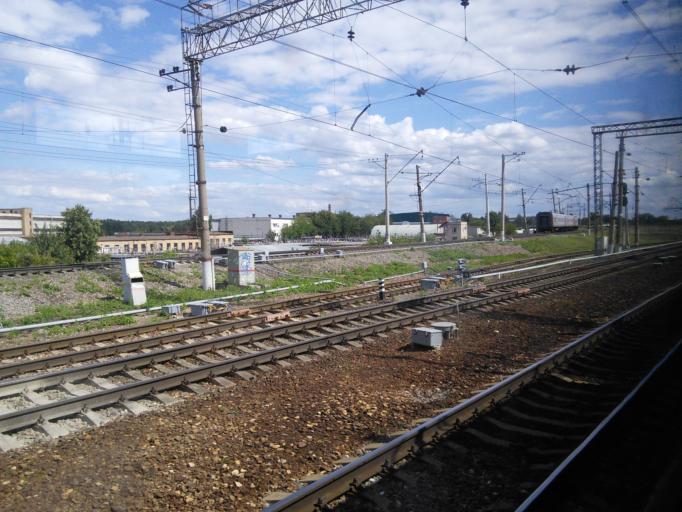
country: RU
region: Moscow
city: Nekrasovka
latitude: 55.6746
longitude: 37.9120
